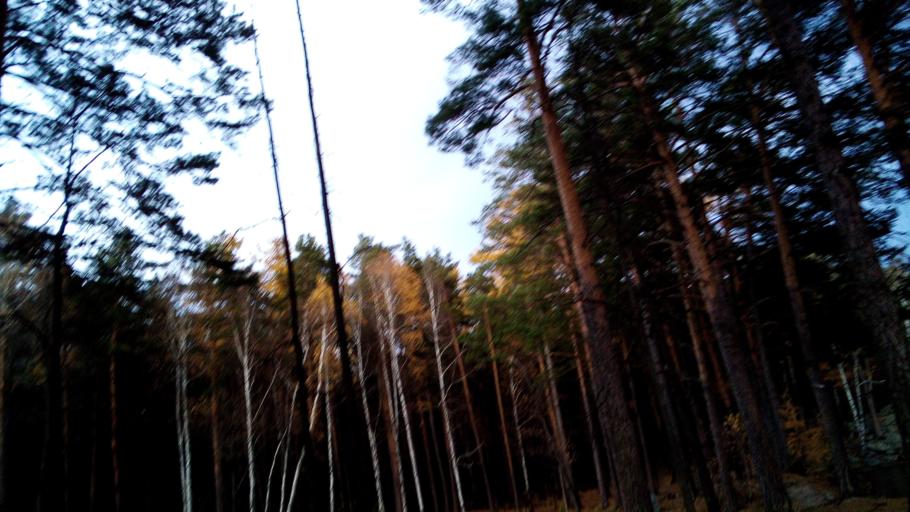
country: RU
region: Chelyabinsk
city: Turgoyak
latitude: 55.1769
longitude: 60.0239
